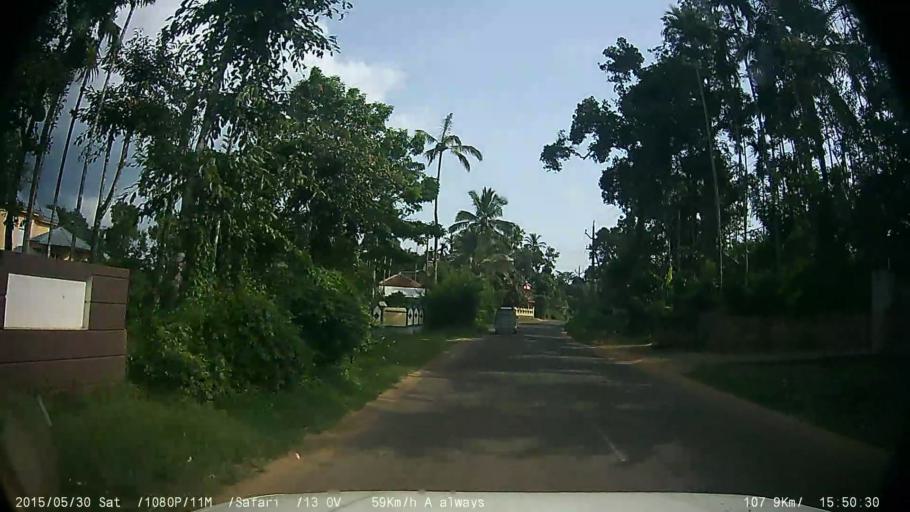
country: IN
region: Kerala
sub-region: Wayanad
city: Panamaram
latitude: 11.6862
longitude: 76.0790
